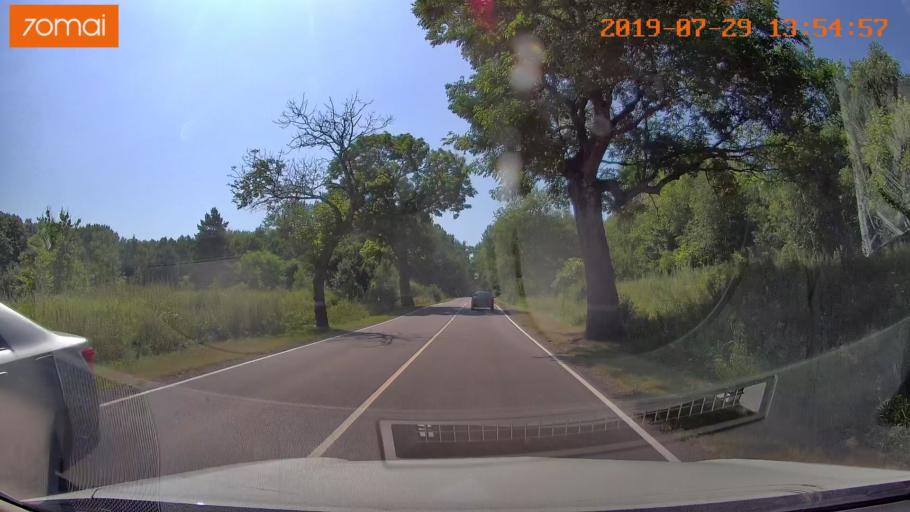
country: RU
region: Kaliningrad
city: Primorsk
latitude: 54.7190
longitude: 19.9615
